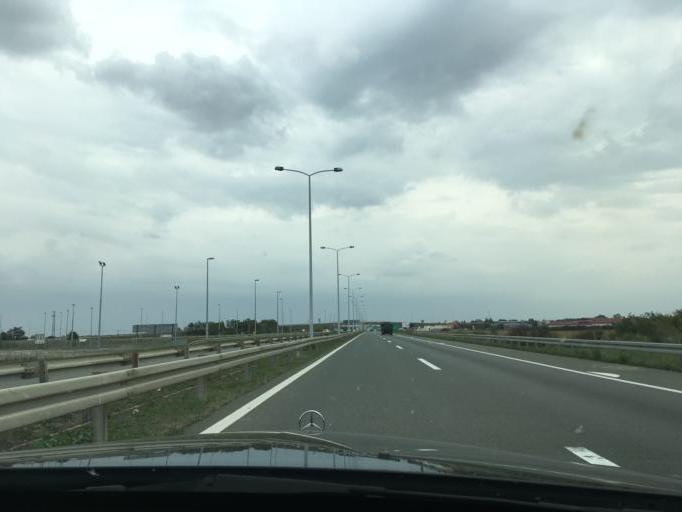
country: RS
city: Dobanovci
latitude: 44.8458
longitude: 20.2048
